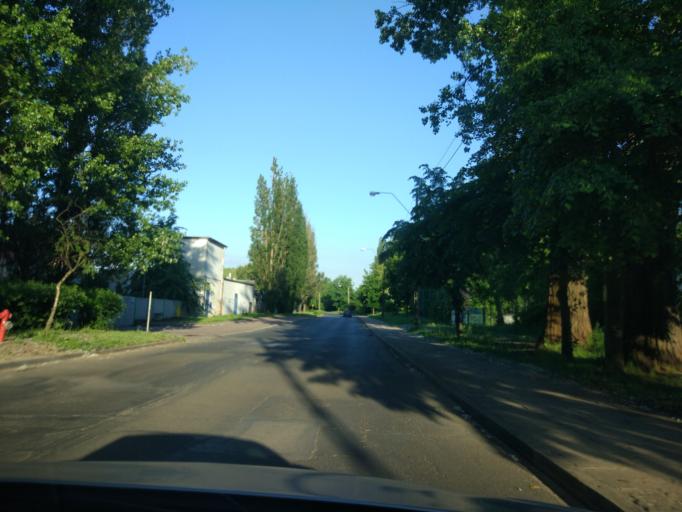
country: PL
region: Lodz Voivodeship
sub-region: Powiat kutnowski
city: Kutno
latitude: 52.2259
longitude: 19.3546
